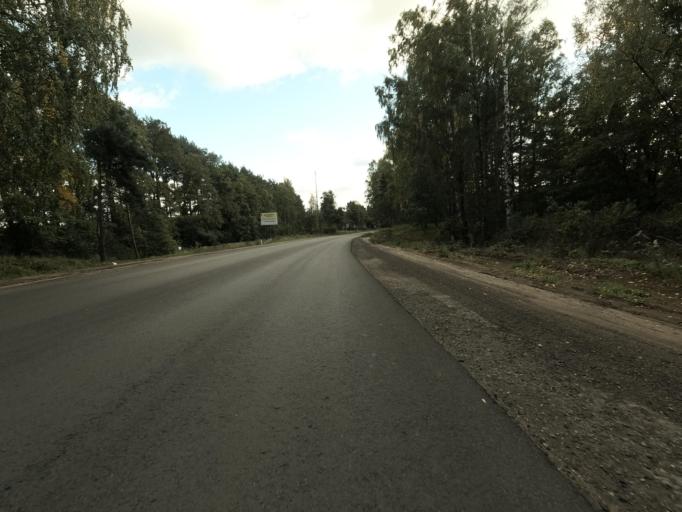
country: RU
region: Leningrad
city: Koltushi
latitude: 59.9484
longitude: 30.6575
